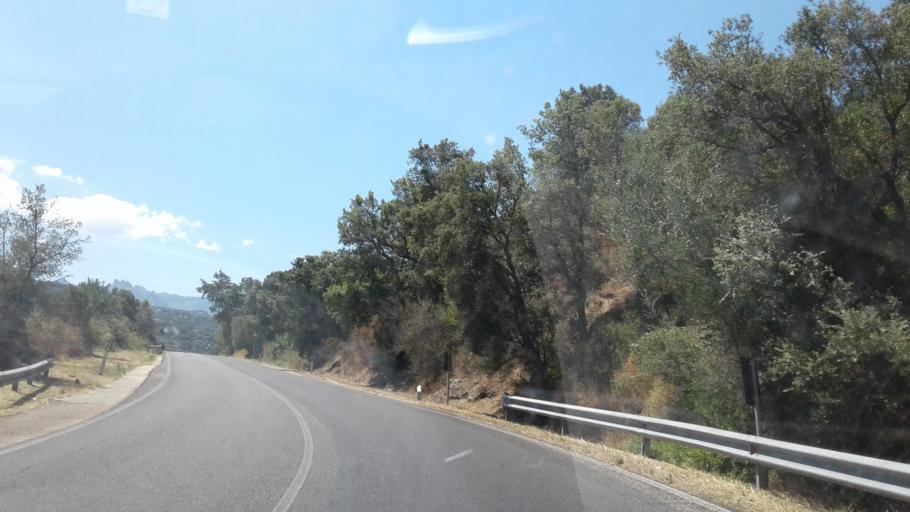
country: IT
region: Sardinia
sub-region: Provincia di Olbia-Tempio
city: Luras
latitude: 40.9446
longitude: 9.1924
